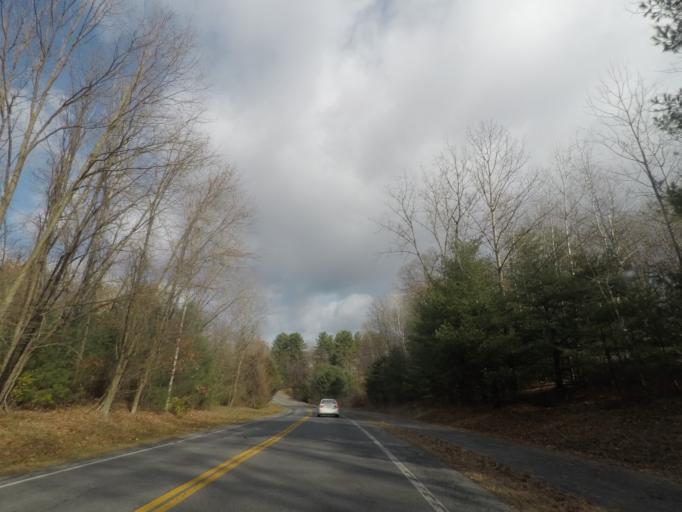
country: US
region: New York
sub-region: Saratoga County
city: Country Knolls
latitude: 42.8965
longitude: -73.7956
